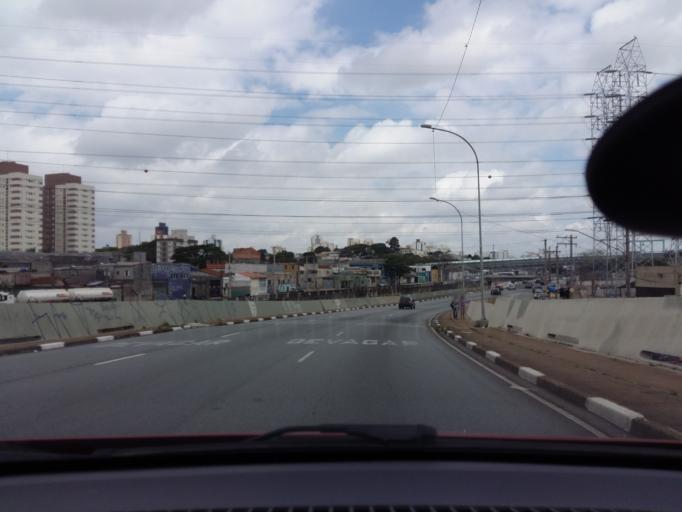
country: BR
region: Sao Paulo
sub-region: Sao Caetano Do Sul
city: Sao Caetano do Sul
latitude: -23.5879
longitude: -46.5905
